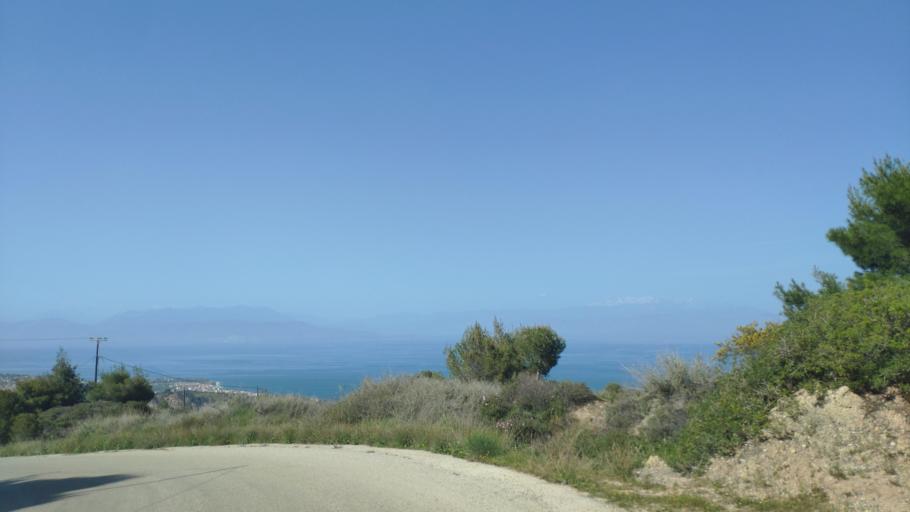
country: GR
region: West Greece
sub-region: Nomos Achaias
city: Aiyira
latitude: 38.1274
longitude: 22.3452
